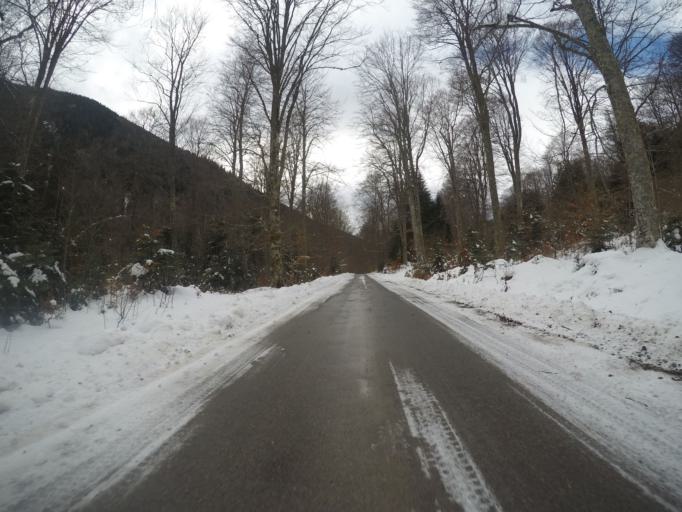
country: BG
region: Kyustendil
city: Sapareva Banya
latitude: 42.1462
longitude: 23.3679
